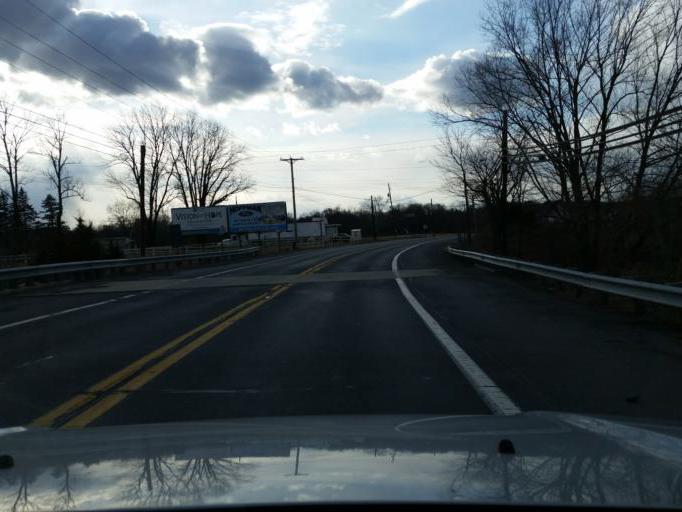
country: US
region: Pennsylvania
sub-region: Dauphin County
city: Middletown
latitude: 40.1967
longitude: -76.7076
